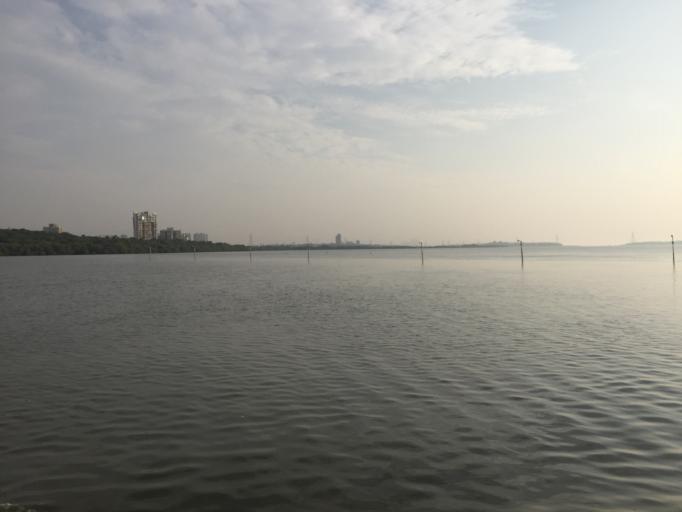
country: IN
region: Maharashtra
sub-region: Mumbai Suburban
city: Borivli
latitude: 19.2250
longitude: 72.8096
